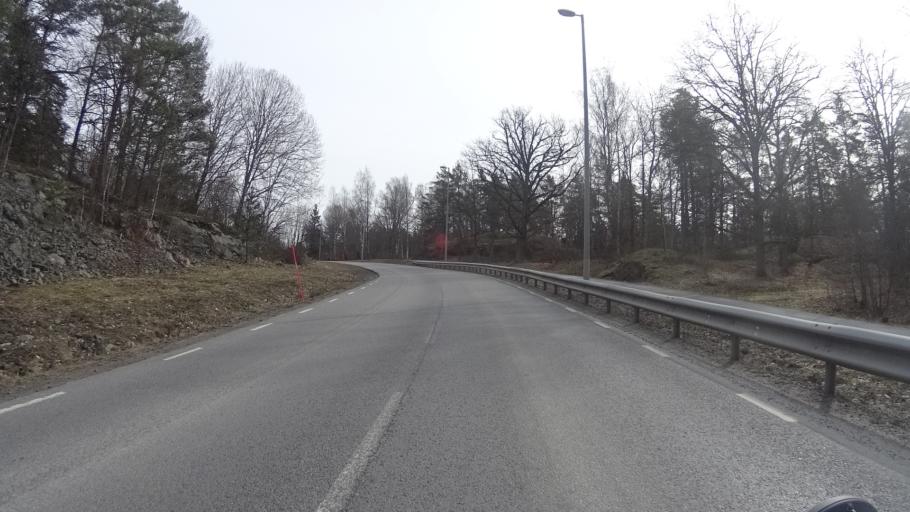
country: SE
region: Stockholm
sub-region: Nacka Kommun
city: Nacka
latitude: 59.2933
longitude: 18.1459
